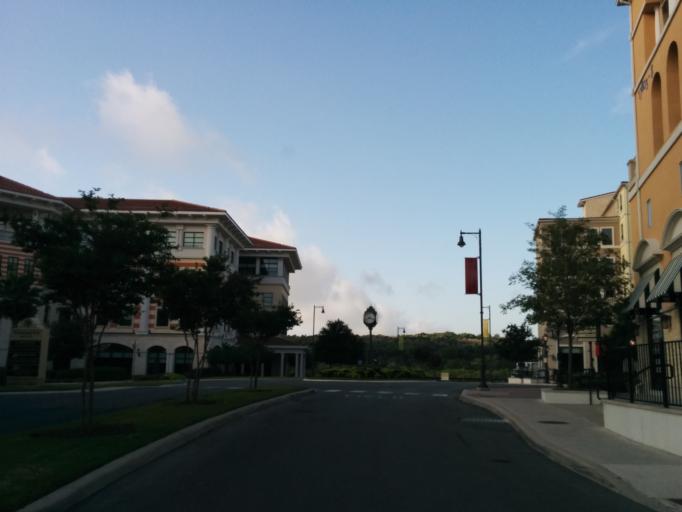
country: US
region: Texas
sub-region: Bexar County
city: Shavano Park
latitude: 29.6105
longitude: -98.6058
